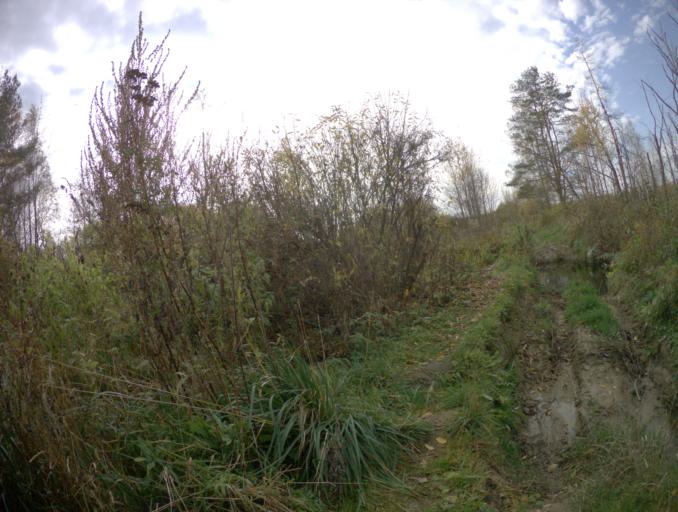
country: RU
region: Vladimir
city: Golovino
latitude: 55.9726
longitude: 40.3867
